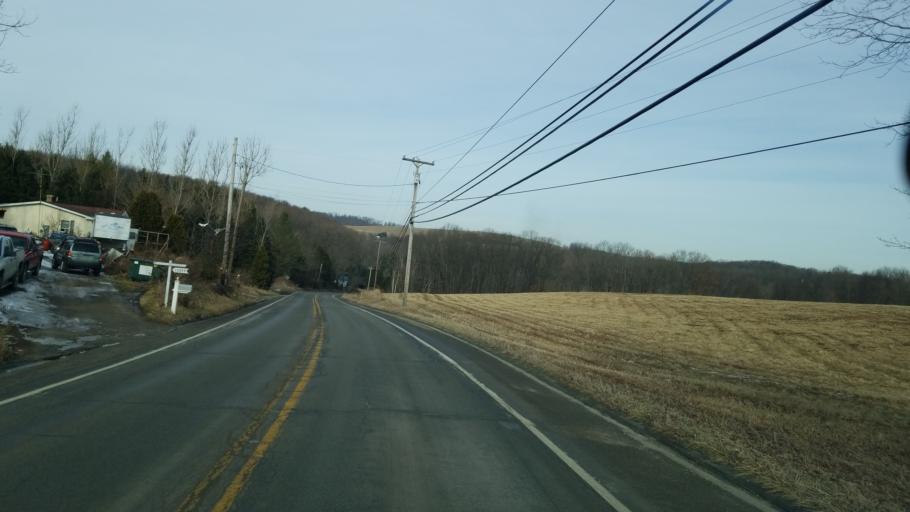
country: US
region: Pennsylvania
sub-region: Indiana County
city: Clymer
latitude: 40.7266
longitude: -78.9353
